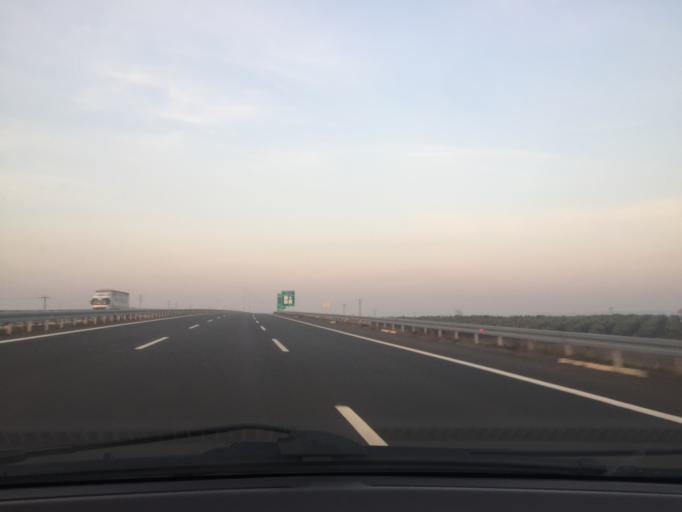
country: TR
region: Bursa
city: Mahmudiye
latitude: 40.2708
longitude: 28.6183
